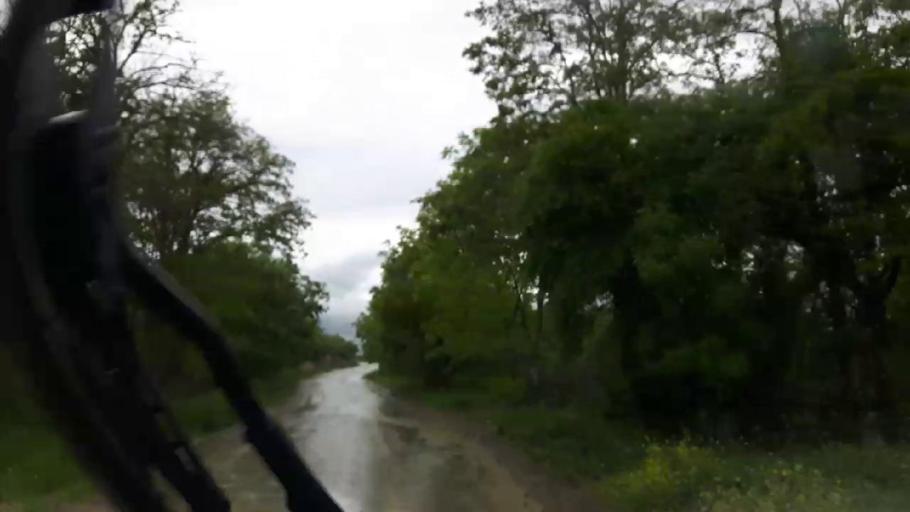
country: GE
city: Agara
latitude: 41.9934
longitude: 43.7360
